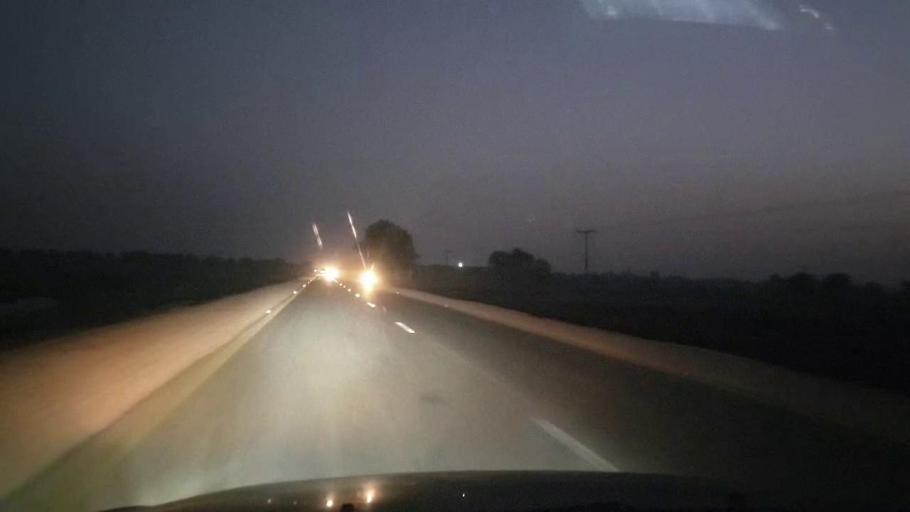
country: PK
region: Sindh
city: Chambar
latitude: 25.3287
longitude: 68.7991
